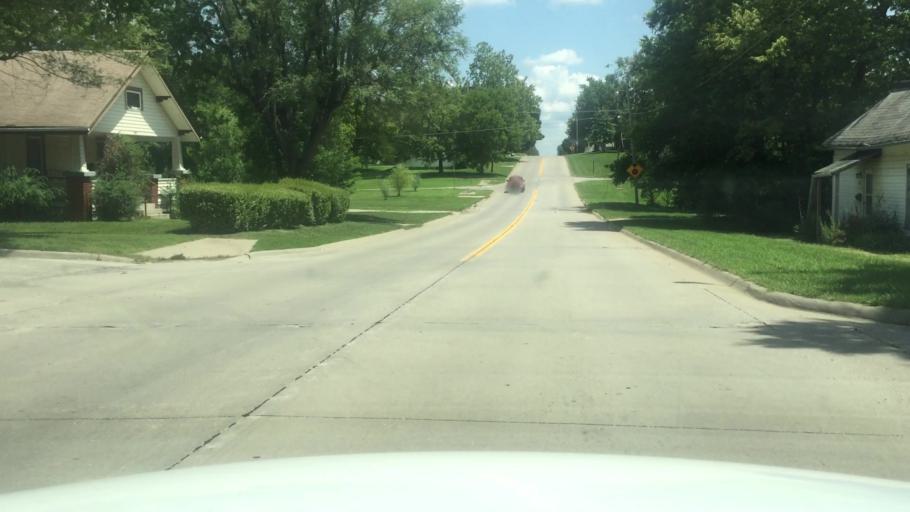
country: US
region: Kansas
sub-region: Brown County
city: Horton
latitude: 39.6673
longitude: -95.5332
